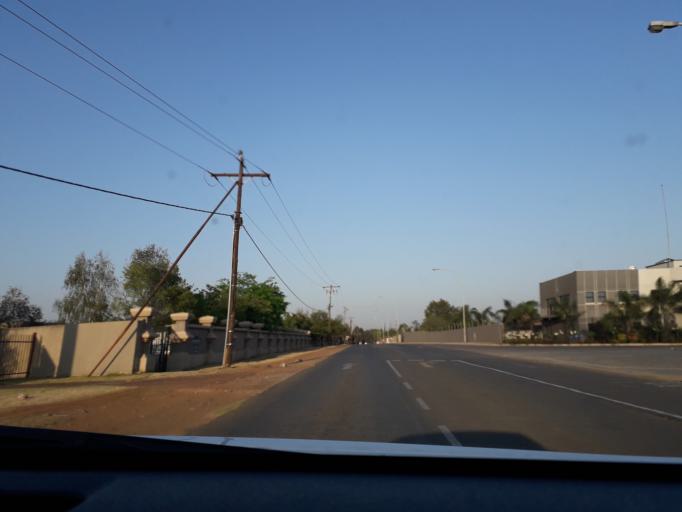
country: ZA
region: Gauteng
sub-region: Ekurhuleni Metropolitan Municipality
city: Benoni
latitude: -26.1102
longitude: 28.3001
